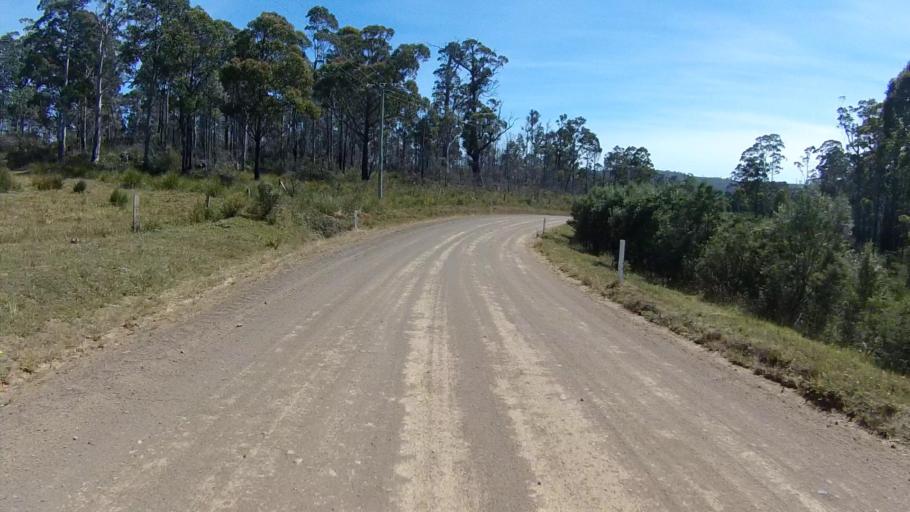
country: AU
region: Tasmania
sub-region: Sorell
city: Sorell
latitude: -42.7293
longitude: 147.7396
